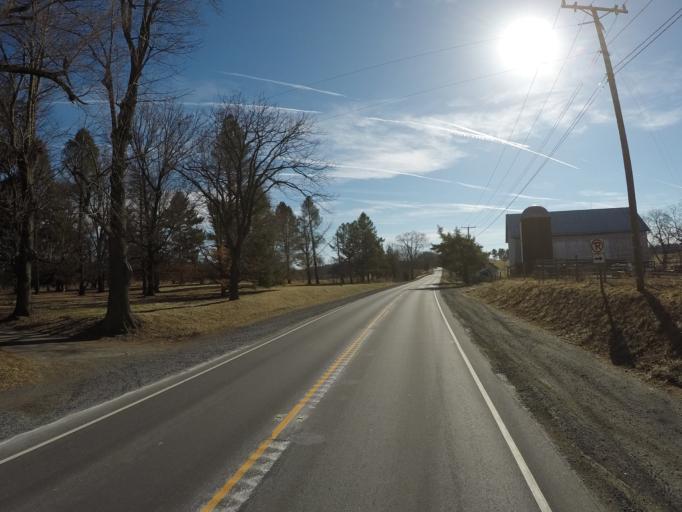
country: US
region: Virginia
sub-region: Loudoun County
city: Leesburg
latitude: 39.1863
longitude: -77.5351
